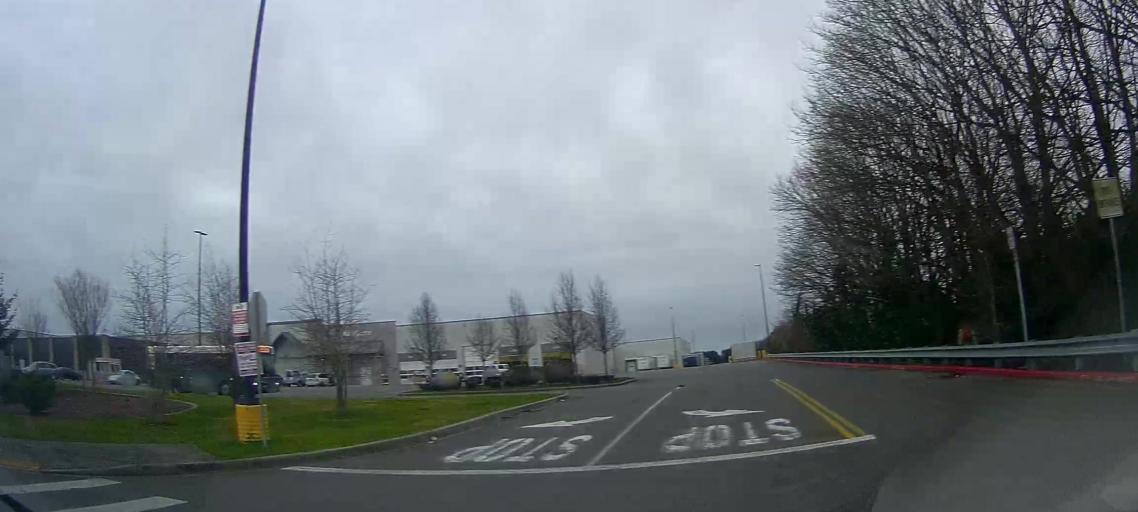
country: US
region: Washington
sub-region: Skagit County
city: Mount Vernon
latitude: 48.4431
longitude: -122.3474
